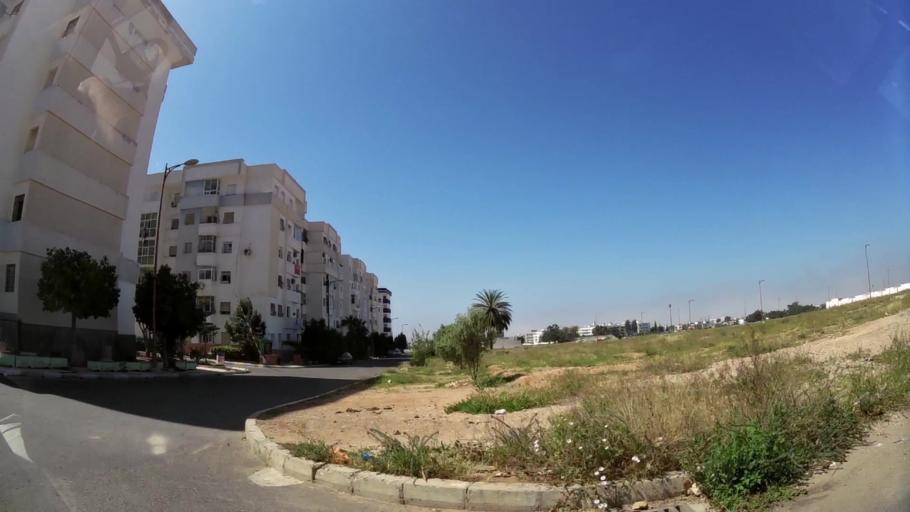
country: MA
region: Oued ed Dahab-Lagouira
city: Dakhla
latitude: 30.4327
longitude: -9.5653
